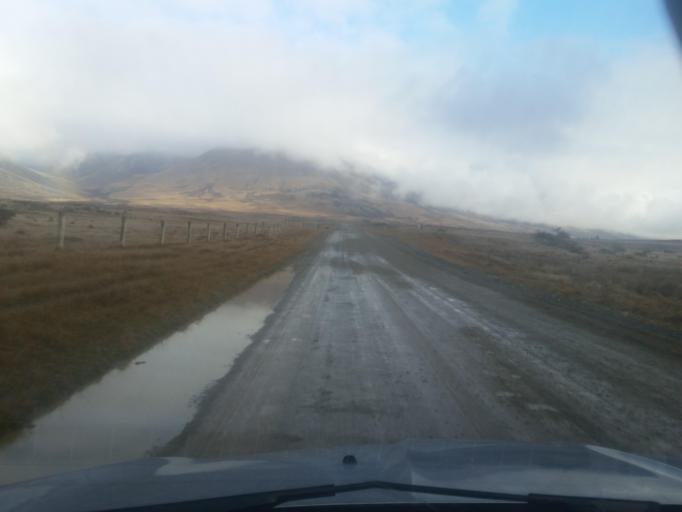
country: NZ
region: Canterbury
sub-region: Ashburton District
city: Methven
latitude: -43.6160
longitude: 171.0898
